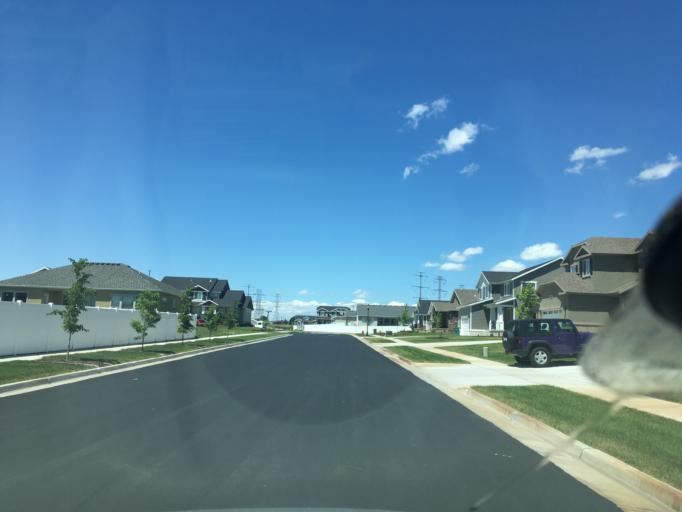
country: US
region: Utah
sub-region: Davis County
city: Layton
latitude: 41.0500
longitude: -112.0057
